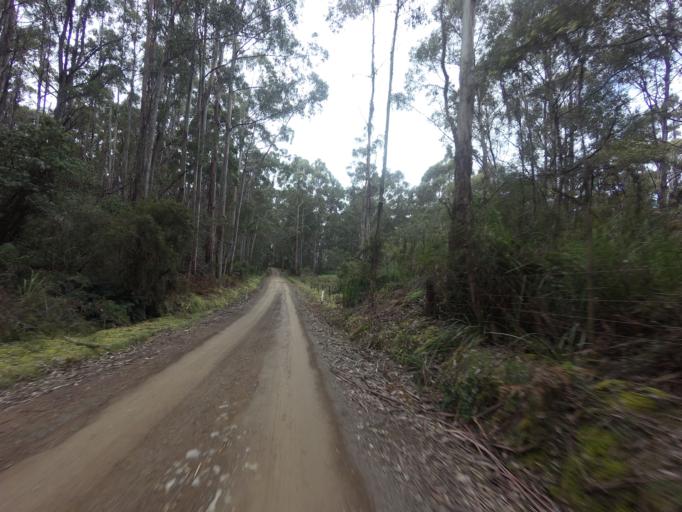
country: AU
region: Tasmania
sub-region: Huon Valley
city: Geeveston
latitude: -43.4235
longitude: 147.0090
